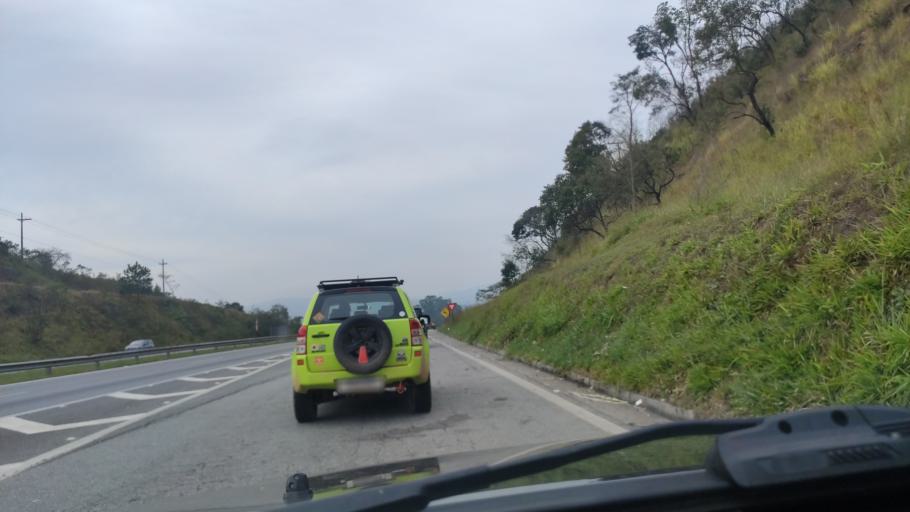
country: BR
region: Sao Paulo
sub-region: Bom Jesus Dos Perdoes
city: Bom Jesus dos Perdoes
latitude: -23.1094
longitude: -46.4978
